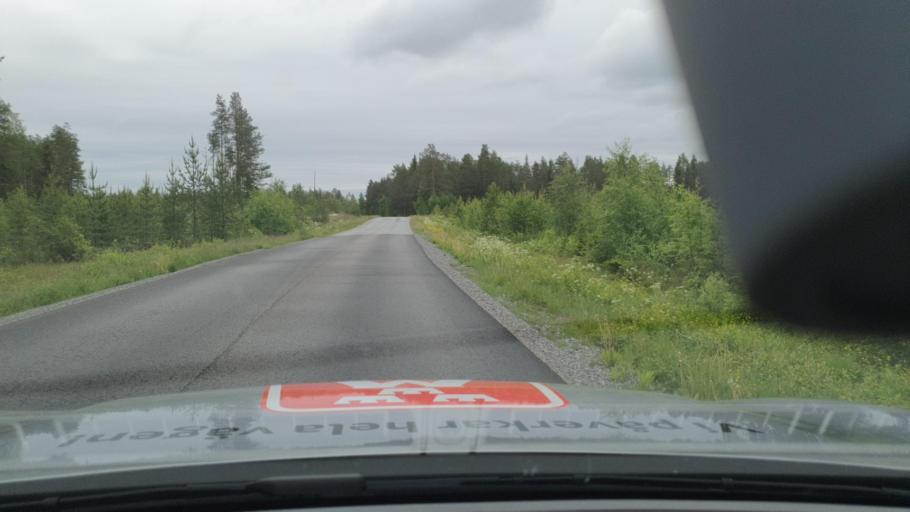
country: SE
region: Norrbotten
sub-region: Lulea Kommun
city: Ranea
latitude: 65.8375
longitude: 22.3011
